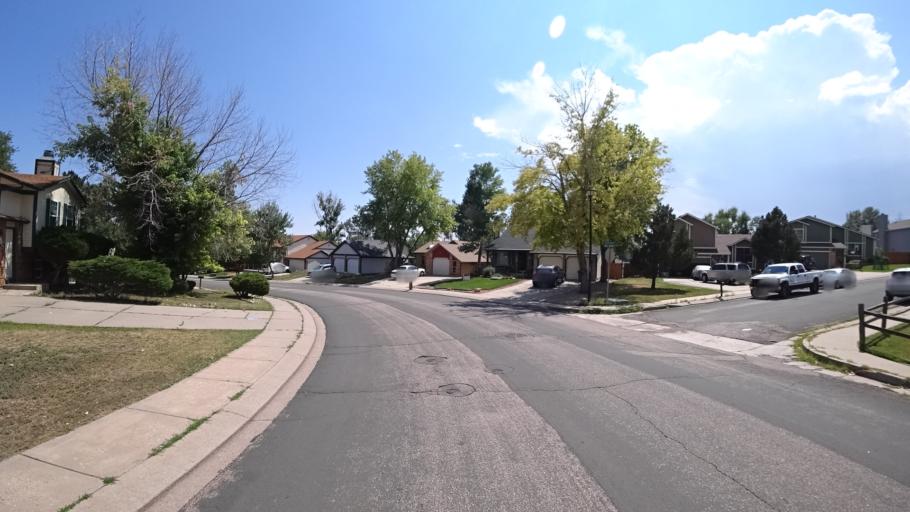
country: US
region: Colorado
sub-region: El Paso County
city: Air Force Academy
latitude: 38.9328
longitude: -104.8686
